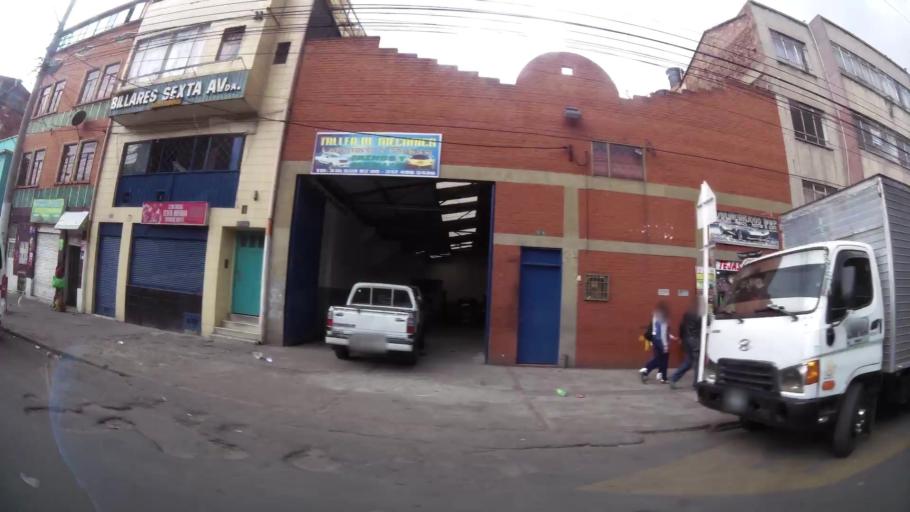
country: CO
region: Bogota D.C.
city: Bogota
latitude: 4.5974
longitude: -74.0902
